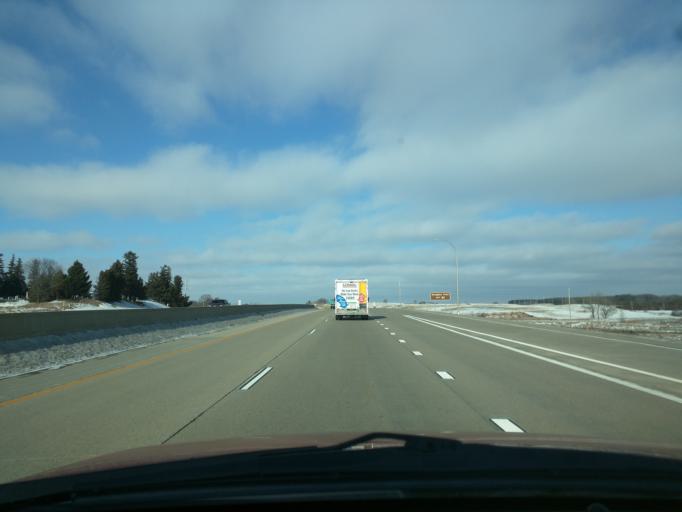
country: US
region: Minnesota
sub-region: Olmsted County
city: Oronoco
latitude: 44.0982
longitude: -92.5122
